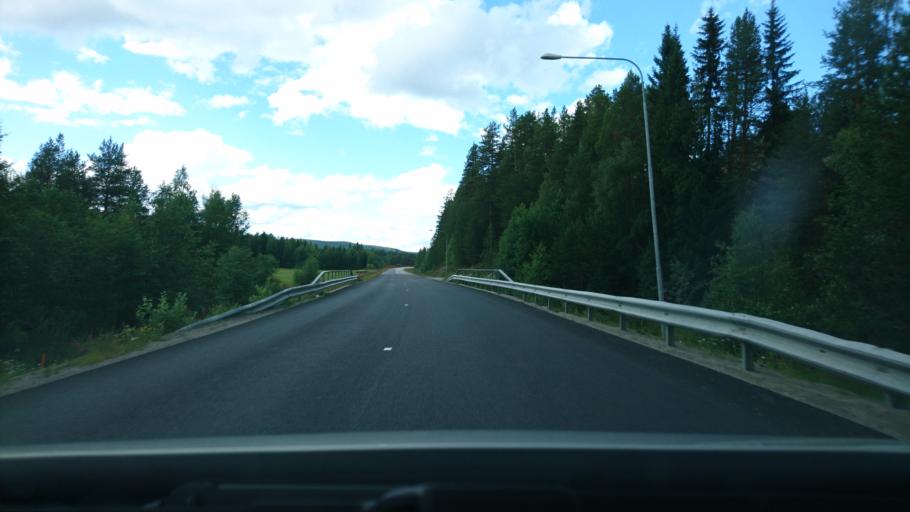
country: SE
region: Vaesterbotten
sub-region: Asele Kommun
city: Asele
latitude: 63.9434
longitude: 17.2825
